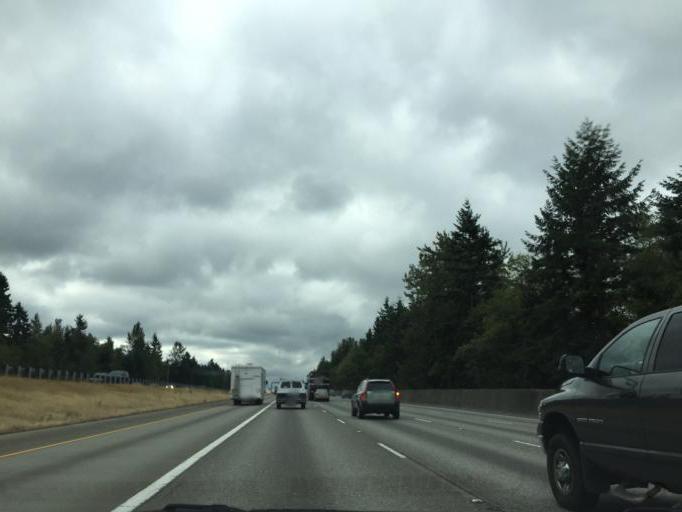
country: US
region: Washington
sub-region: King County
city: Lakeland North
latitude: 47.3382
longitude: -122.2934
